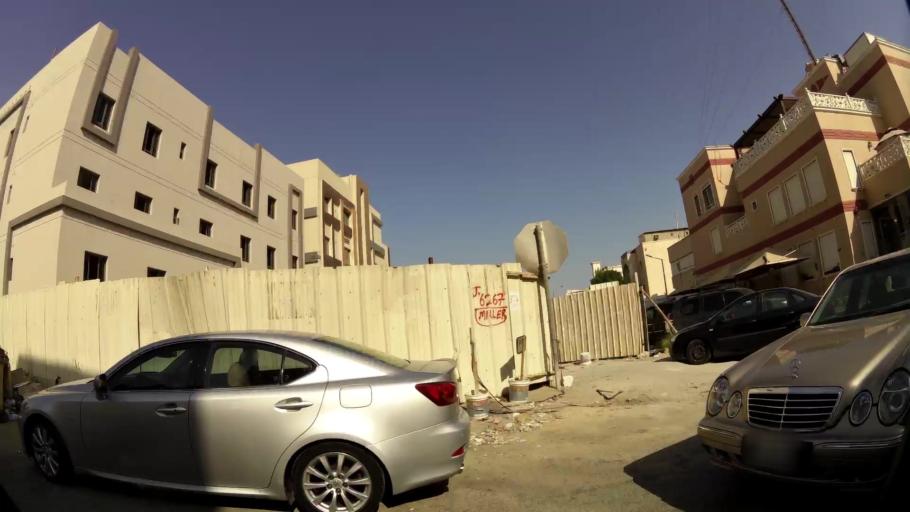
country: KW
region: Muhafazat Hawalli
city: Salwa
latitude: 29.2917
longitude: 48.0813
